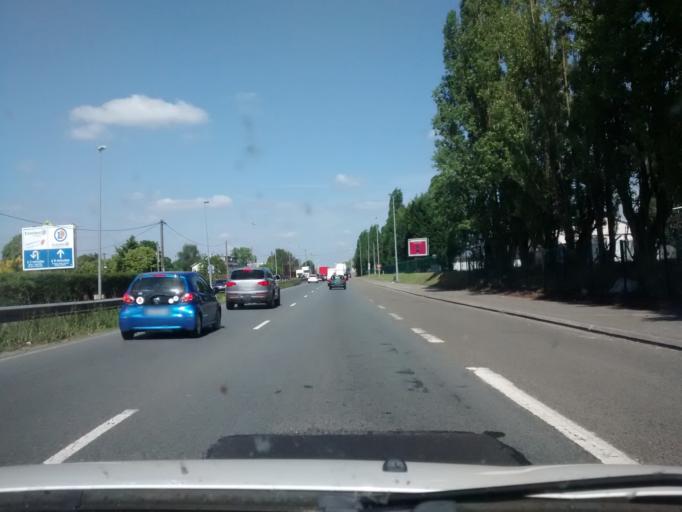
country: FR
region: Ile-de-France
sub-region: Departement des Yvelines
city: Trappes
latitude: 48.7702
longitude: 1.9854
